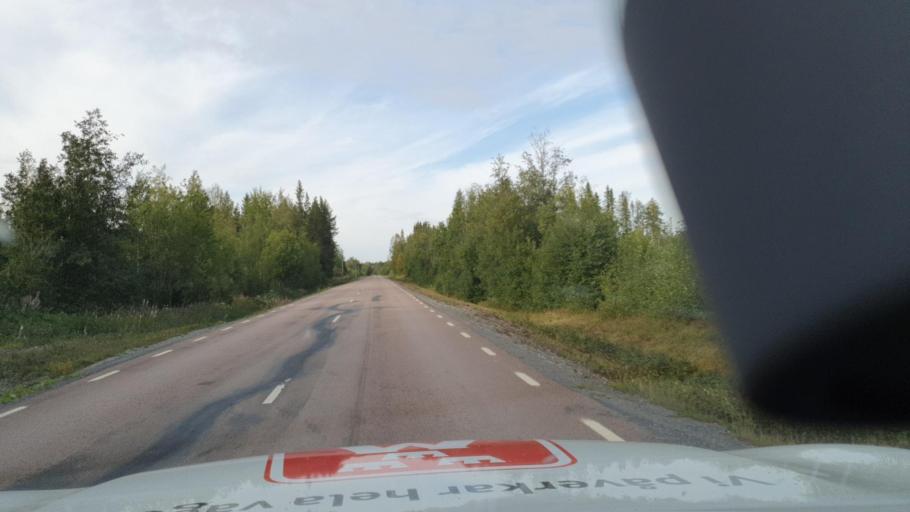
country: SE
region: Jaemtland
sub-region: Stroemsunds Kommun
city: Stroemsund
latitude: 63.7711
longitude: 15.7102
